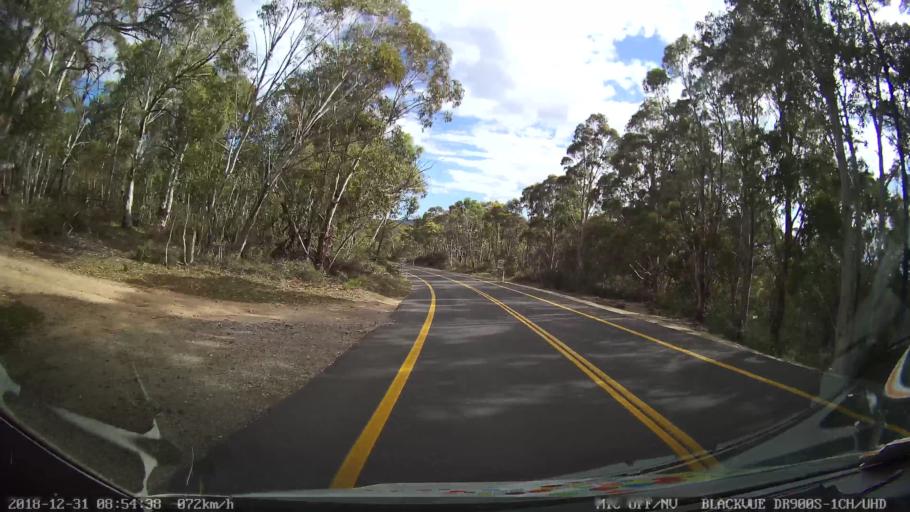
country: AU
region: New South Wales
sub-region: Snowy River
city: Jindabyne
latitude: -36.3527
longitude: 148.5633
